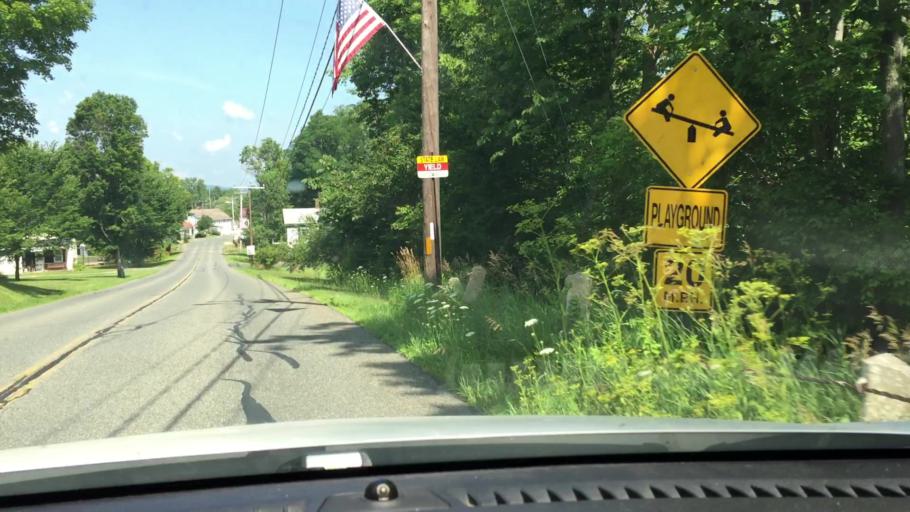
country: US
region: Massachusetts
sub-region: Berkshire County
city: Lee
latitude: 42.2442
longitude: -73.2017
